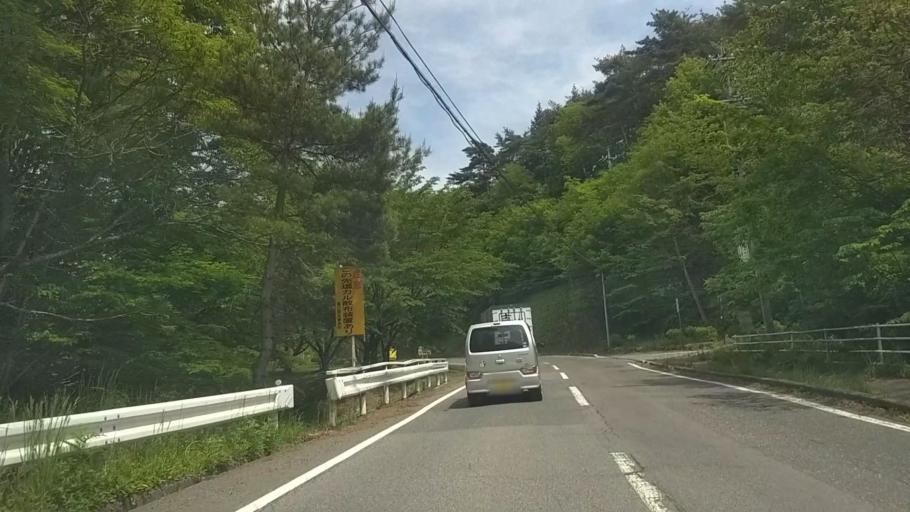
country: JP
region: Nagano
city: Chino
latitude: 35.9348
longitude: 138.2100
